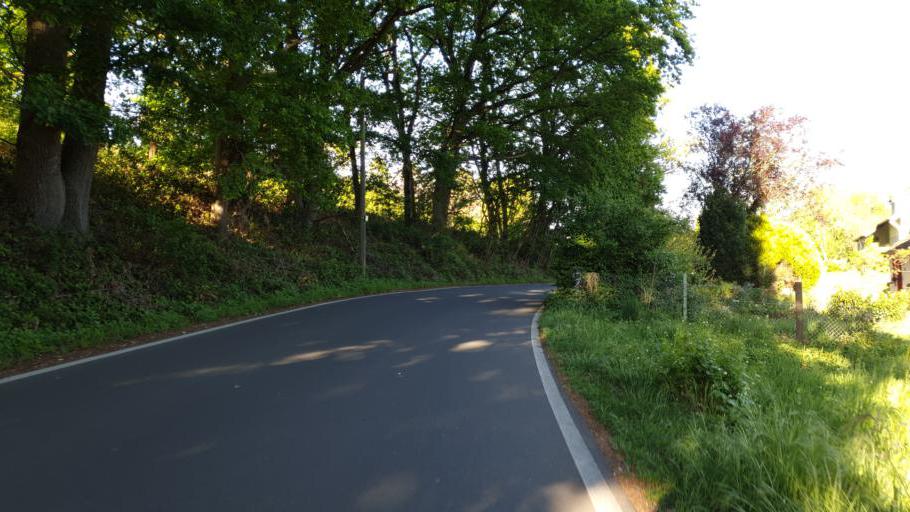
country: DE
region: North Rhine-Westphalia
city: Opladen
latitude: 51.0682
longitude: 7.0527
